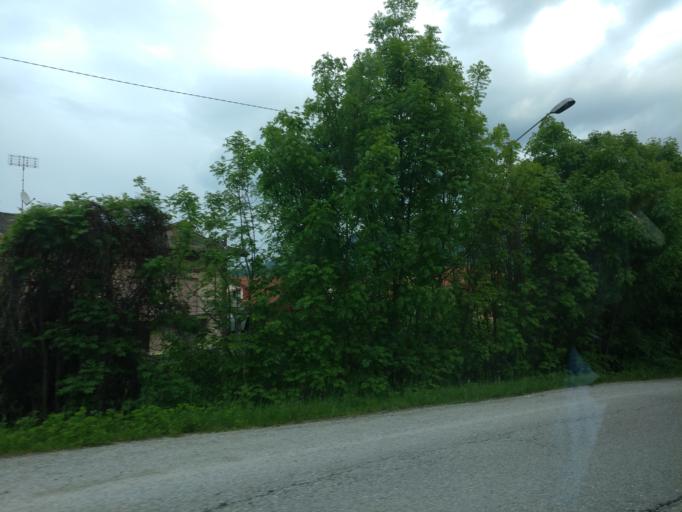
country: IT
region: Piedmont
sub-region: Provincia di Cuneo
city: Paesana
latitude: 44.6769
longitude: 7.2796
